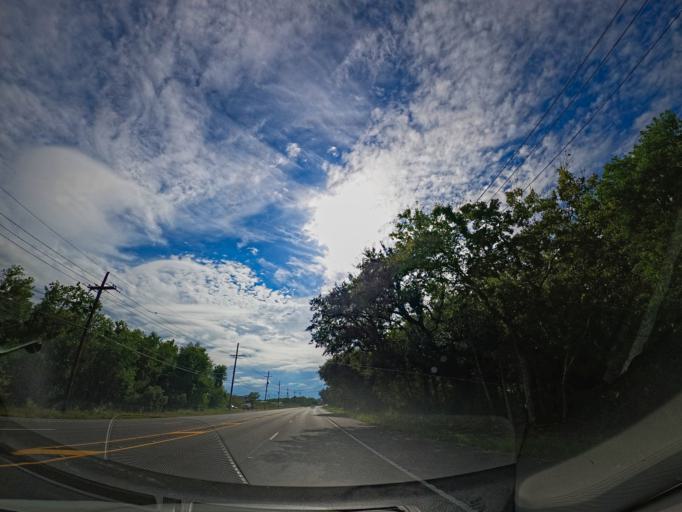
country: US
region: Louisiana
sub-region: Saint Bernard Parish
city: Meraux
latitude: 30.0571
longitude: -89.8723
